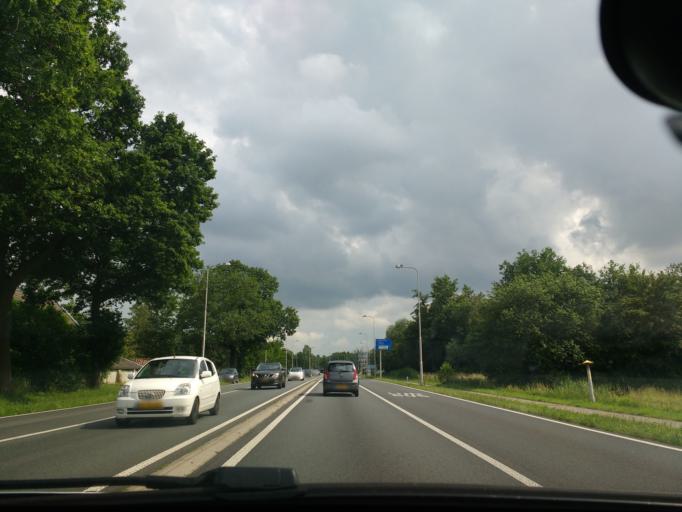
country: NL
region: Gelderland
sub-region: Gemeente Ede
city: Bennekom
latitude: 51.9897
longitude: 5.6676
